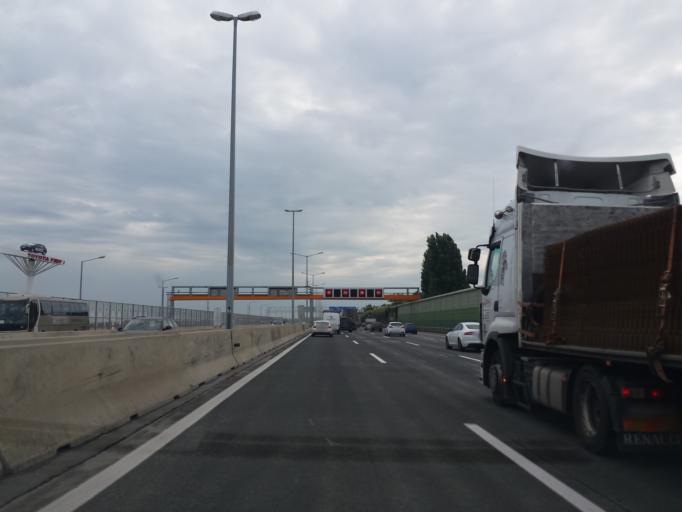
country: AT
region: Lower Austria
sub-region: Politischer Bezirk Modling
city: Vosendorf
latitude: 48.1379
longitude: 16.3323
